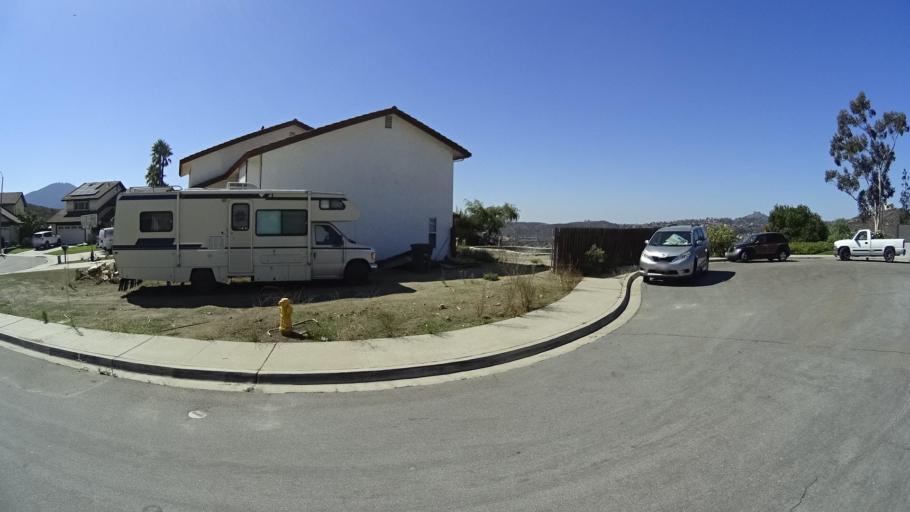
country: US
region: California
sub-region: San Diego County
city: Rancho San Diego
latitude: 32.7521
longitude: -116.9208
